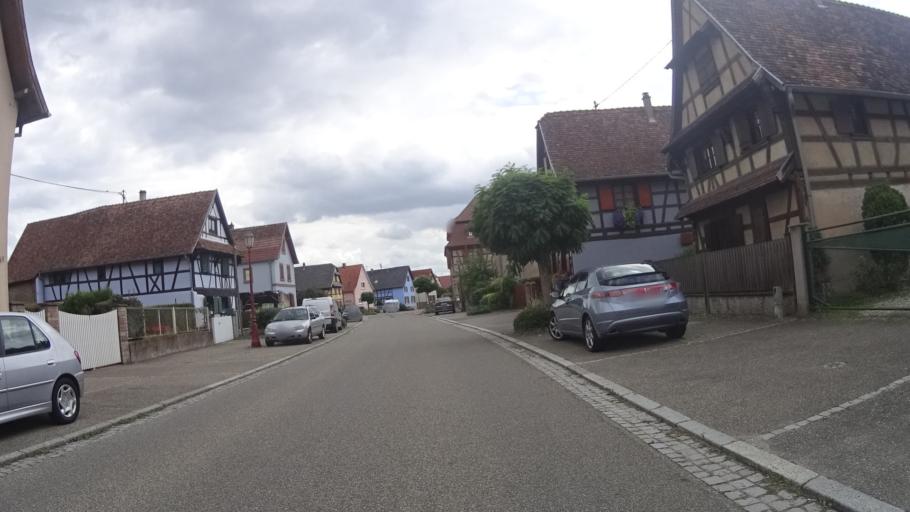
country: FR
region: Alsace
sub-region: Departement du Bas-Rhin
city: Weyersheim
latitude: 48.7172
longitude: 7.8034
